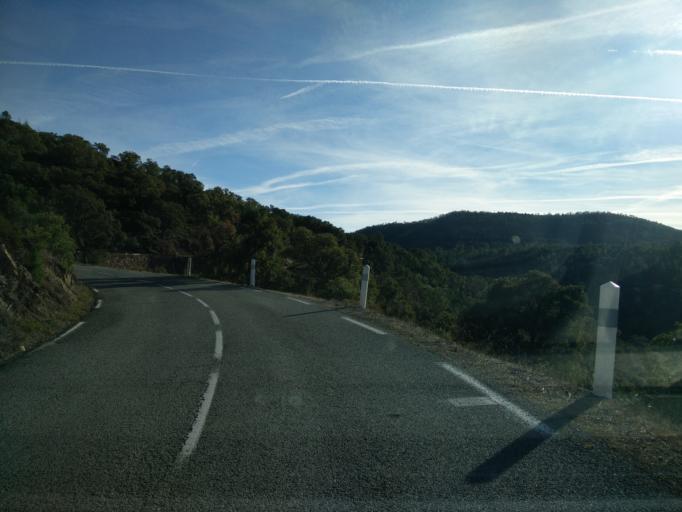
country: FR
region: Provence-Alpes-Cote d'Azur
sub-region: Departement du Var
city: Saint-Raphael
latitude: 43.5027
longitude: 6.7863
